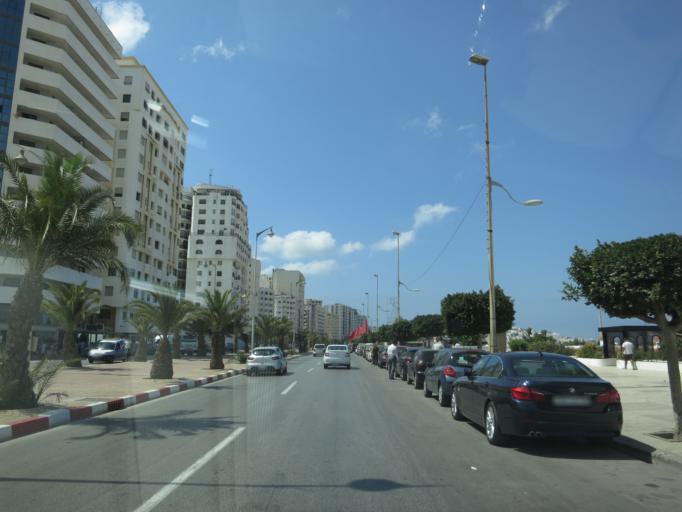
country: MA
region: Tanger-Tetouan
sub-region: Tanger-Assilah
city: Tangier
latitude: 35.7763
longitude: -5.7951
